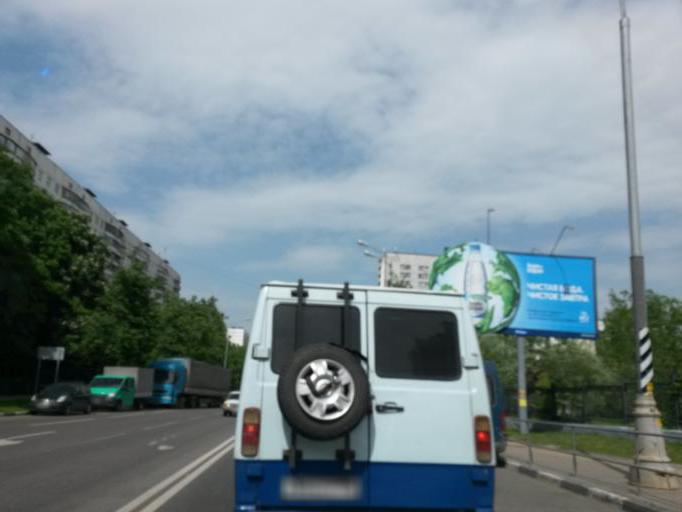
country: RU
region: Moscow
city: Chertanovo Yuzhnoye
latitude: 55.5961
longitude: 37.5963
